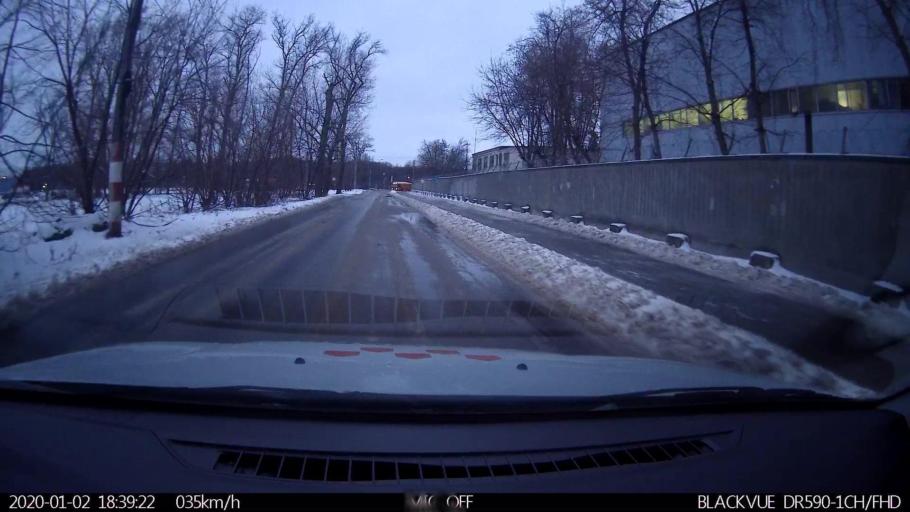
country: RU
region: Nizjnij Novgorod
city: Gorbatovka
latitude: 56.3297
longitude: 43.8598
